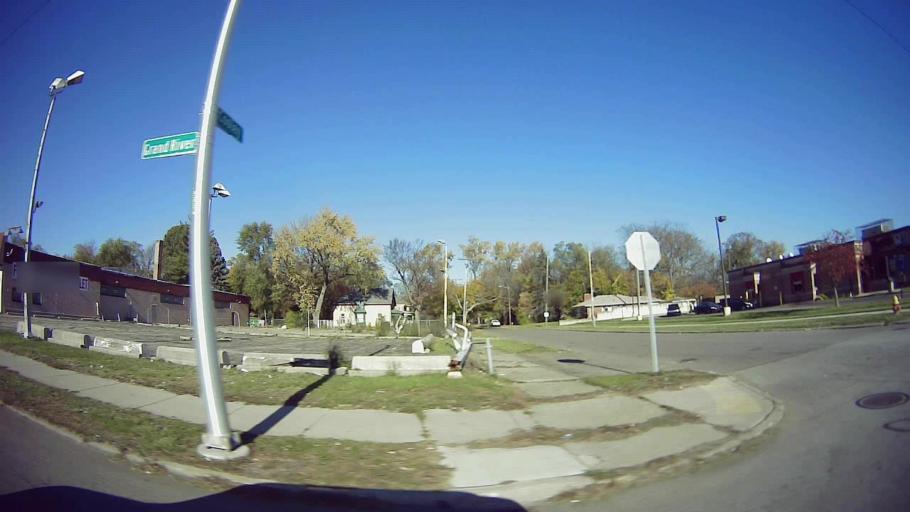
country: US
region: Michigan
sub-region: Wayne County
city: Redford
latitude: 42.4179
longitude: -83.2610
